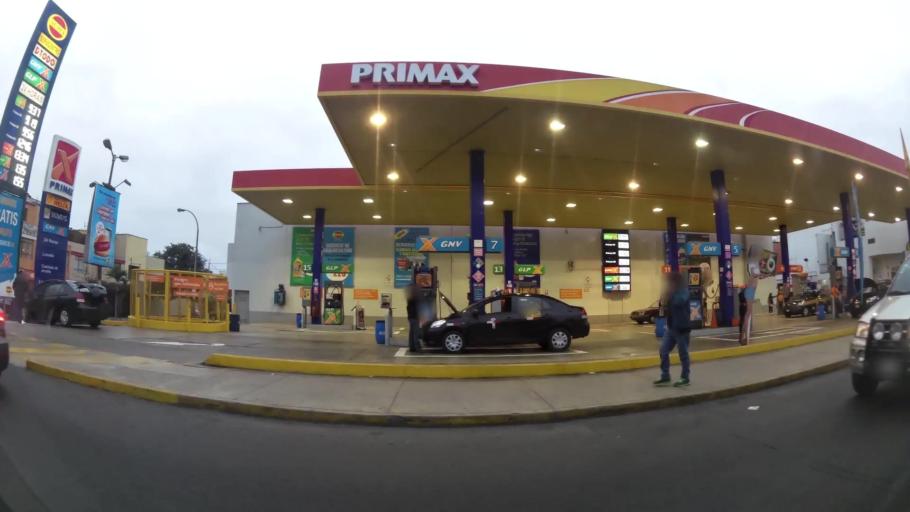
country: PE
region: Lima
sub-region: Lima
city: San Isidro
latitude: -12.0818
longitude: -77.0667
